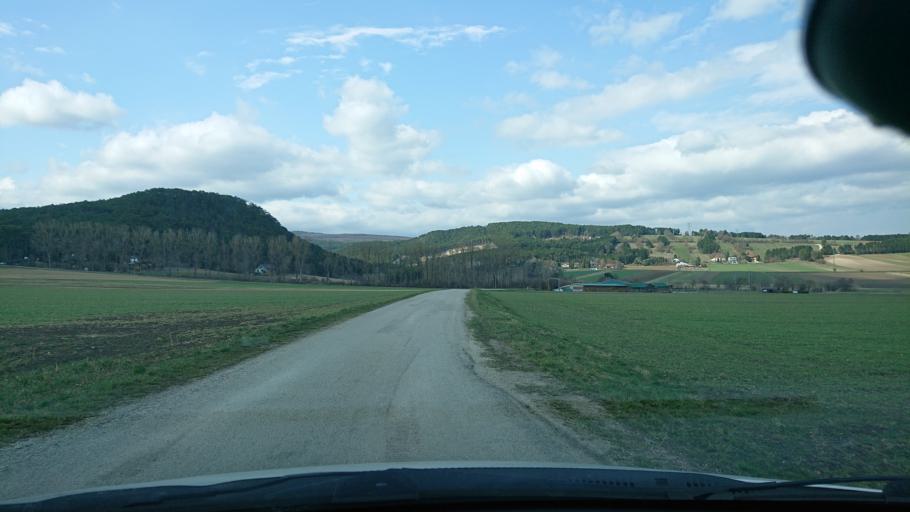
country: AT
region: Lower Austria
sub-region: Politischer Bezirk Baden
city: Berndorf
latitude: 47.9288
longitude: 16.0848
